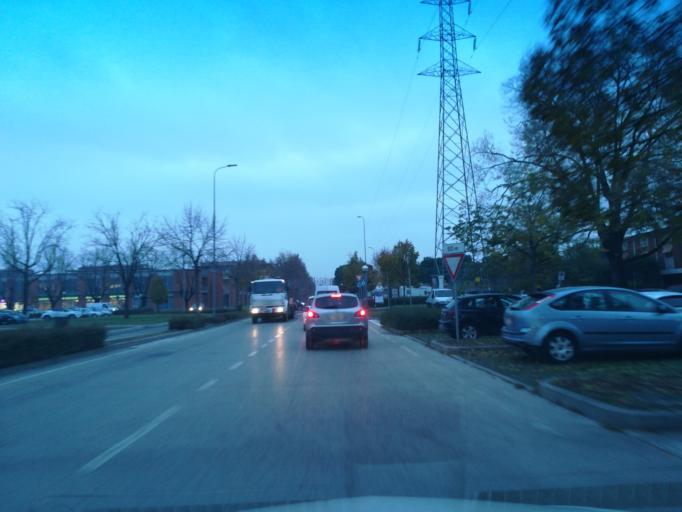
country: IT
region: Emilia-Romagna
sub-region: Provincia di Ravenna
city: Faenza
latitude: 44.2944
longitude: 11.8643
